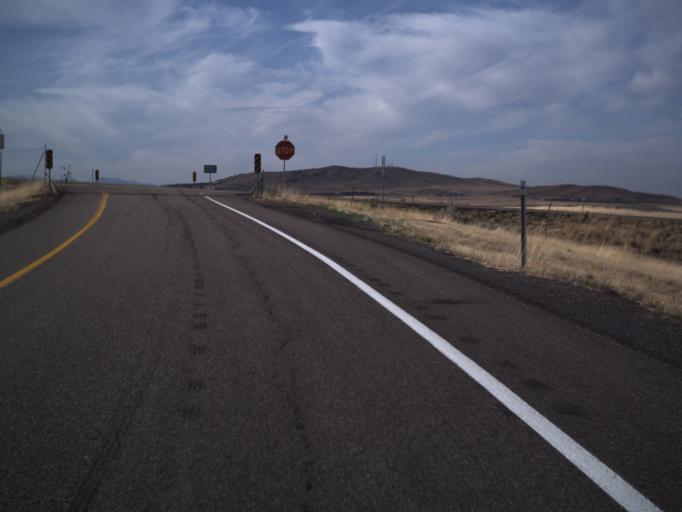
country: US
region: Utah
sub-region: Millard County
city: Fillmore
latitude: 39.0838
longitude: -112.2772
